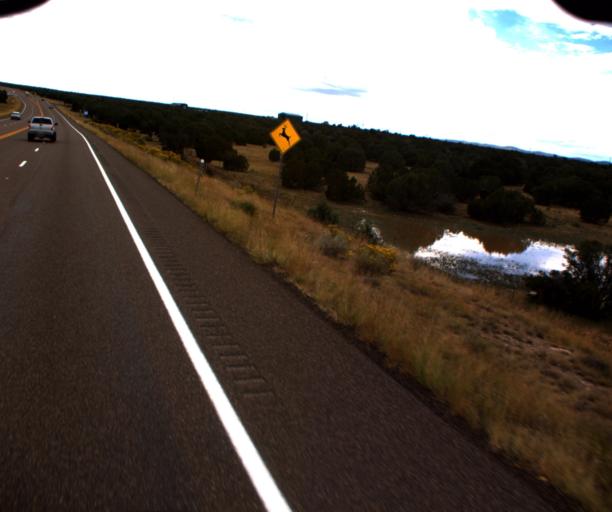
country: US
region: Arizona
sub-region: Navajo County
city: White Mountain Lake
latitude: 34.3644
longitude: -110.0524
